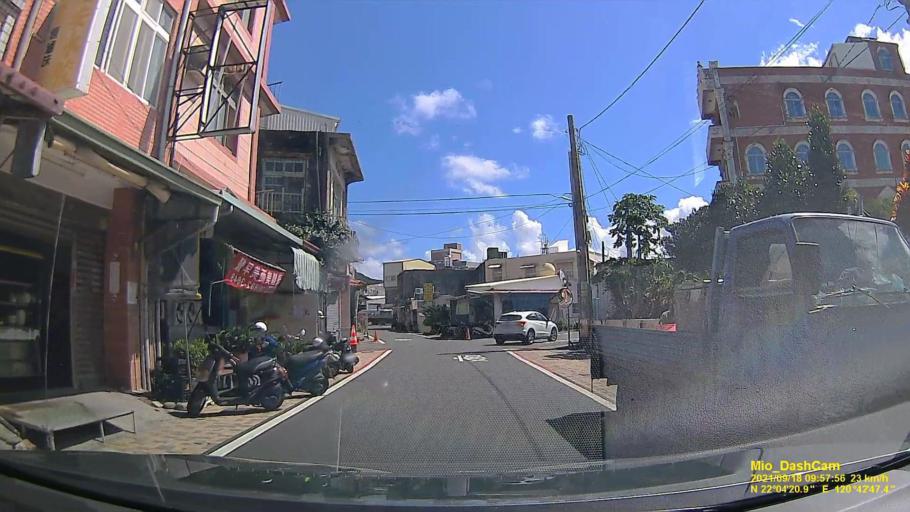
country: TW
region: Taiwan
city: Hengchun
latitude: 22.0725
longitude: 120.7132
